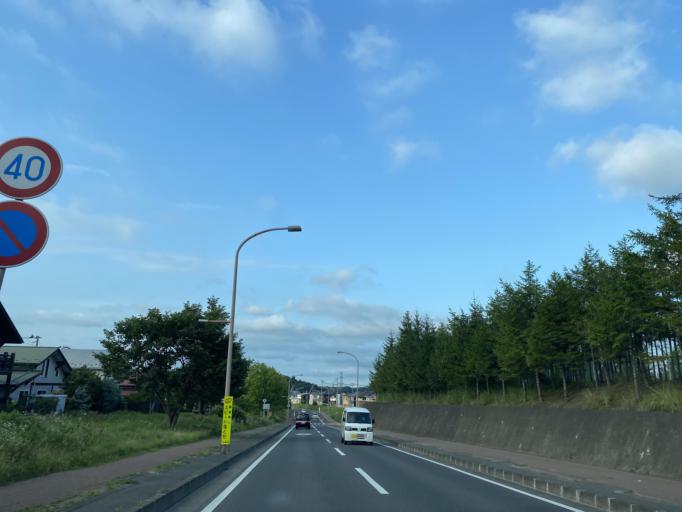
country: JP
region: Miyagi
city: Tomiya
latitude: 38.3825
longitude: 140.8673
